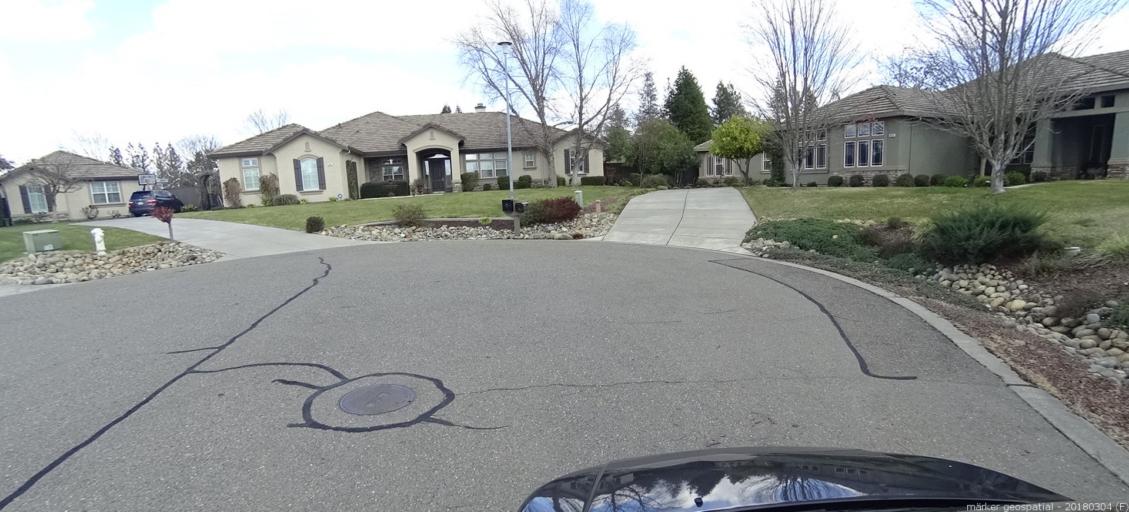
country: US
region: California
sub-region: Sacramento County
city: Vineyard
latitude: 38.4617
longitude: -121.3008
